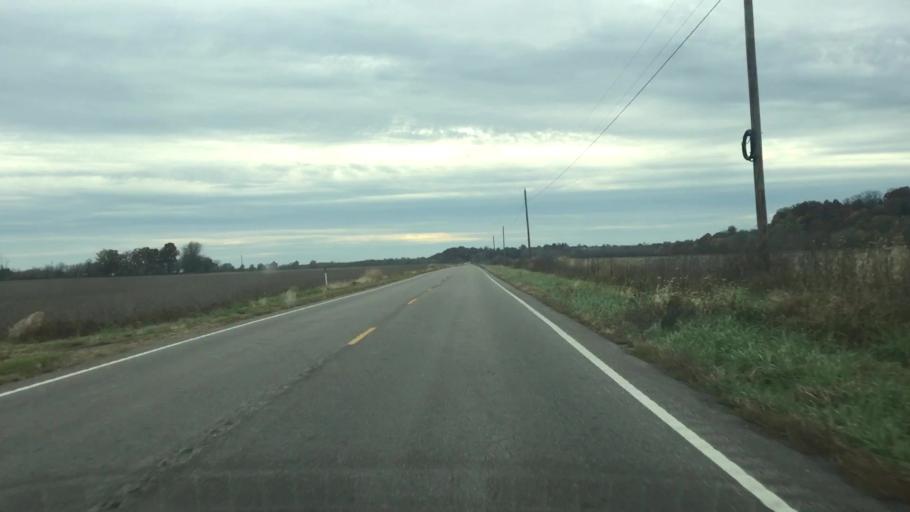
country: US
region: Missouri
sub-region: Callaway County
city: Fulton
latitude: 38.7050
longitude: -91.8012
